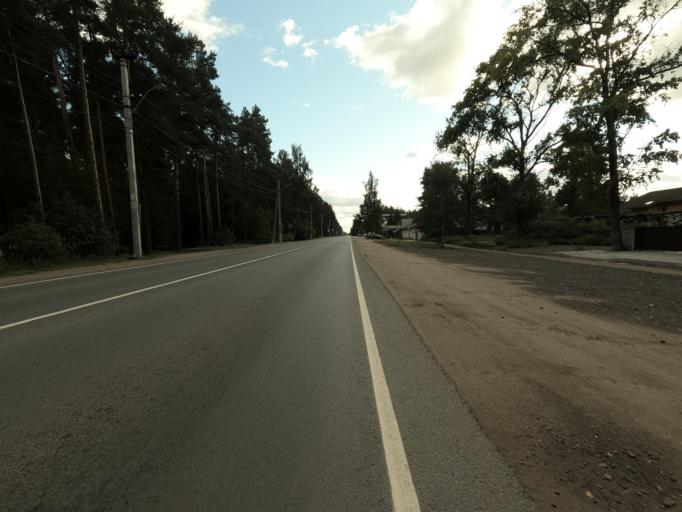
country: RU
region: Leningrad
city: Vsevolozhsk
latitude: 59.9996
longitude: 30.6615
